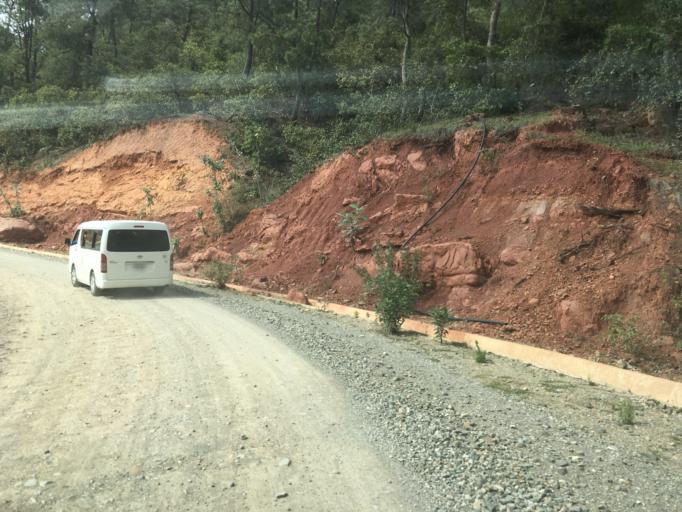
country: MX
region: Oaxaca
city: Santiago Tilantongo
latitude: 17.1999
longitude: -97.2797
